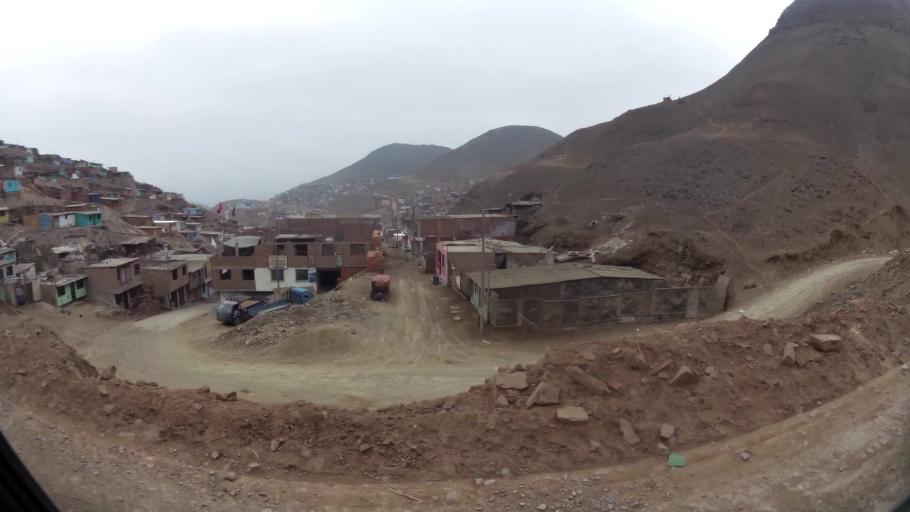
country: PE
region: Lima
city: Ventanilla
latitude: -11.9137
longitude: -77.0932
